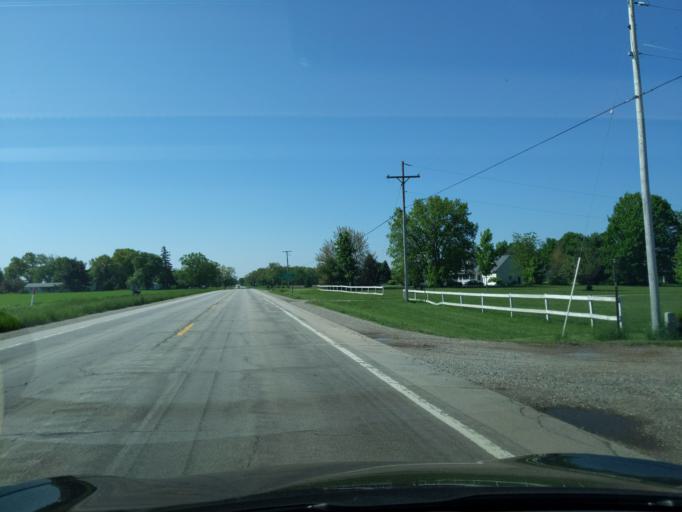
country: US
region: Michigan
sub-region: Ingham County
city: Stockbridge
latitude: 42.5040
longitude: -84.1902
